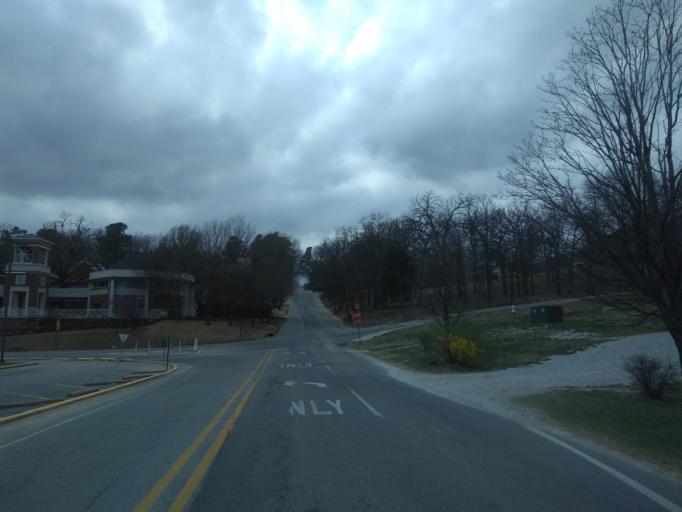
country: US
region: Arkansas
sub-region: Washington County
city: Fayetteville
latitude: 36.0705
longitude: -94.1793
